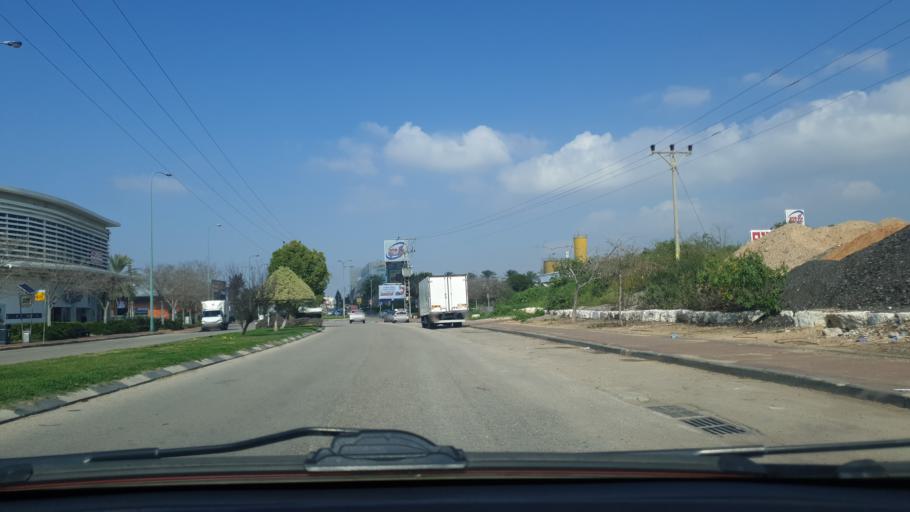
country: IL
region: Tel Aviv
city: Azor
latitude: 32.0066
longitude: 34.8076
